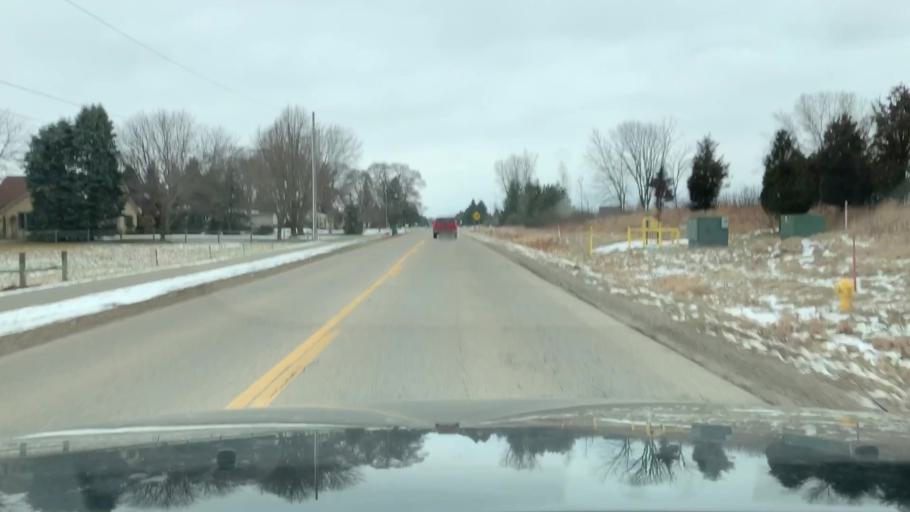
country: US
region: Michigan
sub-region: Ottawa County
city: Zeeland
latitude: 42.7878
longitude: -86.0381
